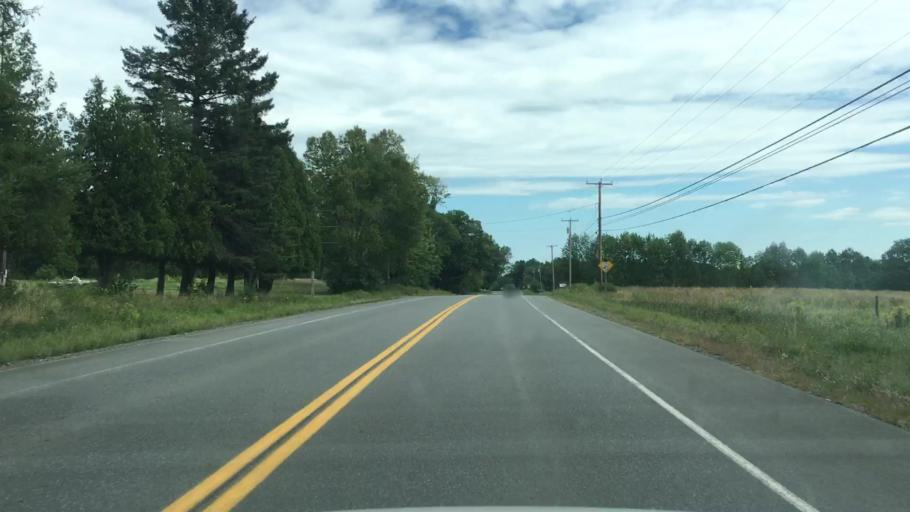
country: US
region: Maine
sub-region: Piscataquis County
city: Milo
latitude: 45.2439
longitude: -69.0138
